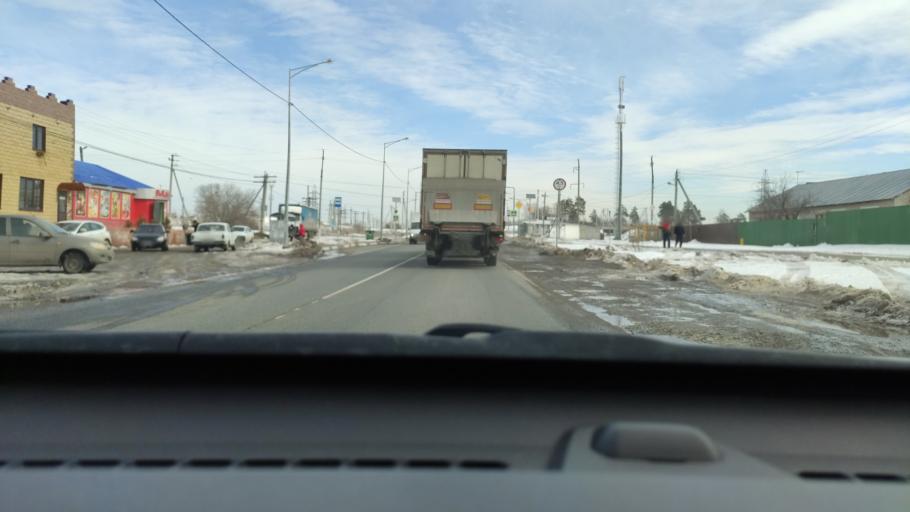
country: RU
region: Samara
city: Zhigulevsk
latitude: 53.5552
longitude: 49.5331
